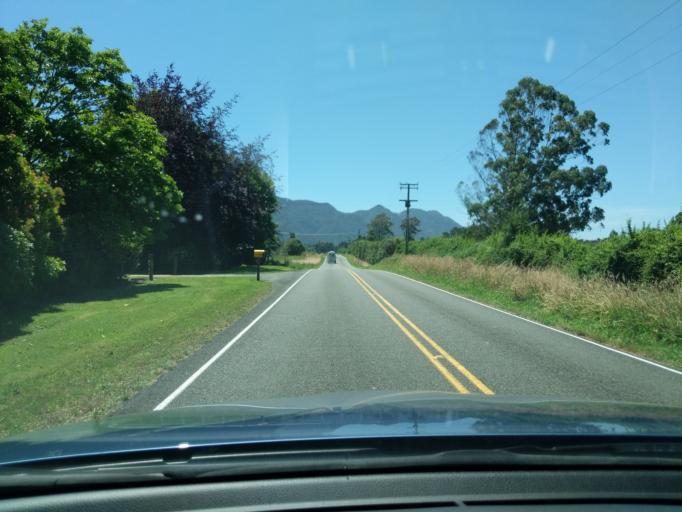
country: NZ
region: Tasman
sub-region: Tasman District
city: Takaka
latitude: -40.7146
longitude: 172.6380
